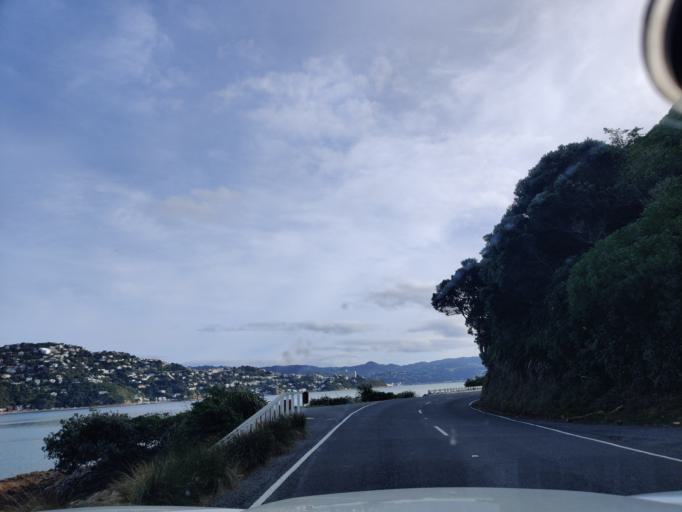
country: NZ
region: Wellington
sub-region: Wellington City
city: Wellington
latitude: -41.3007
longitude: 174.8175
